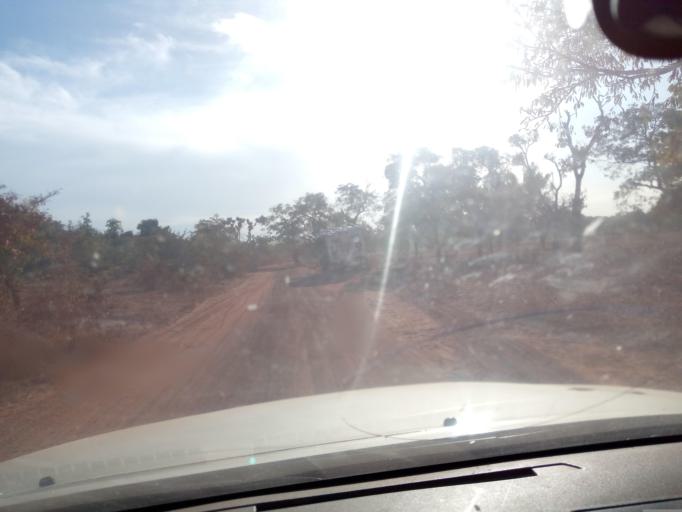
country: ML
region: Sikasso
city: Sikasso
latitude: 11.4248
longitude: -5.5610
